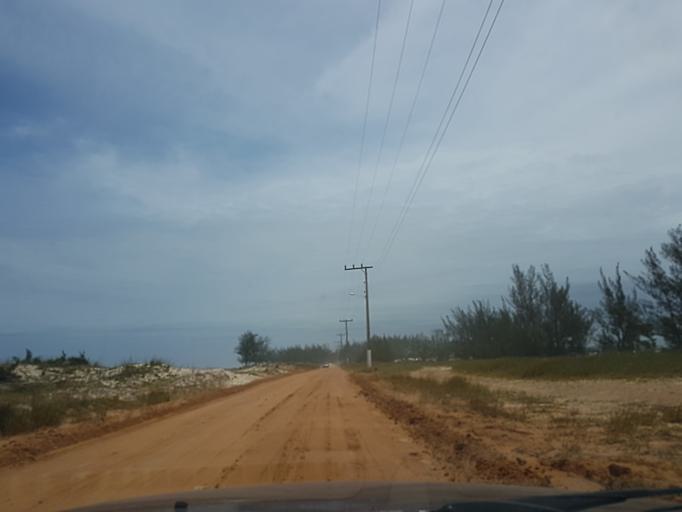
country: BR
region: Santa Catarina
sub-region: Jaguaruna
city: Jaguaruna
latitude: -28.6691
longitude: -48.9718
